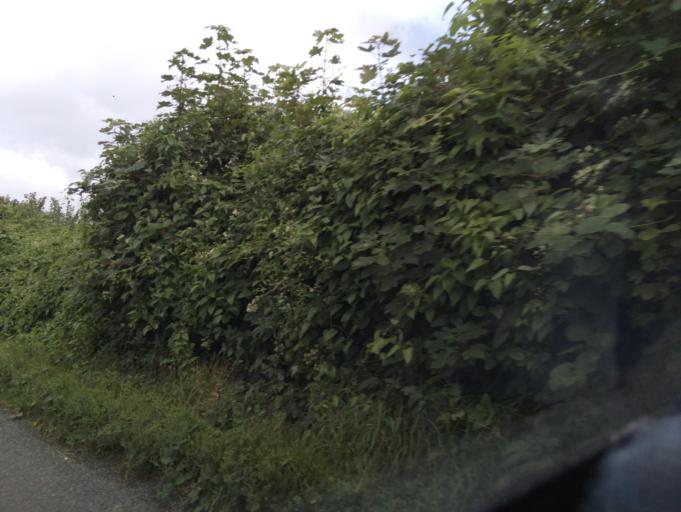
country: GB
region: England
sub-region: Dorset
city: Stalbridge
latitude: 50.9843
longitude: -2.4042
